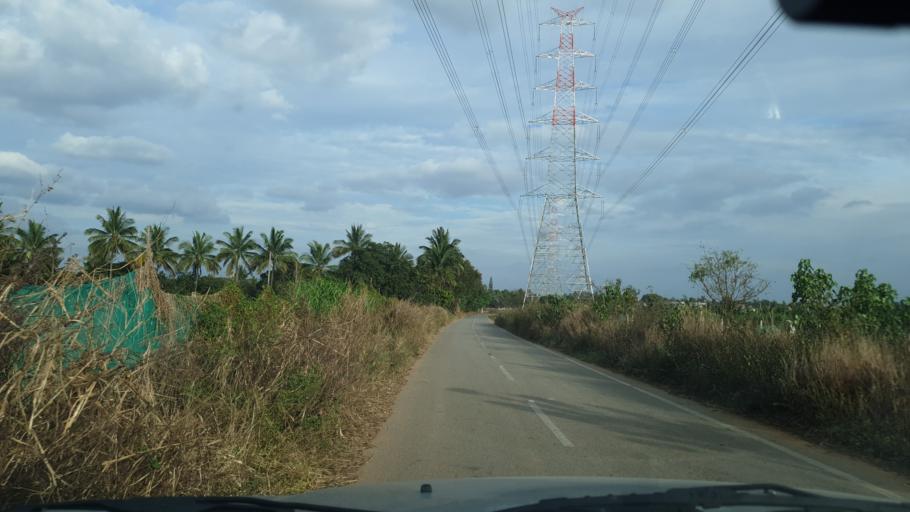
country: IN
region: Karnataka
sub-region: Bangalore Urban
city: Yelahanka
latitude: 13.1973
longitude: 77.6151
